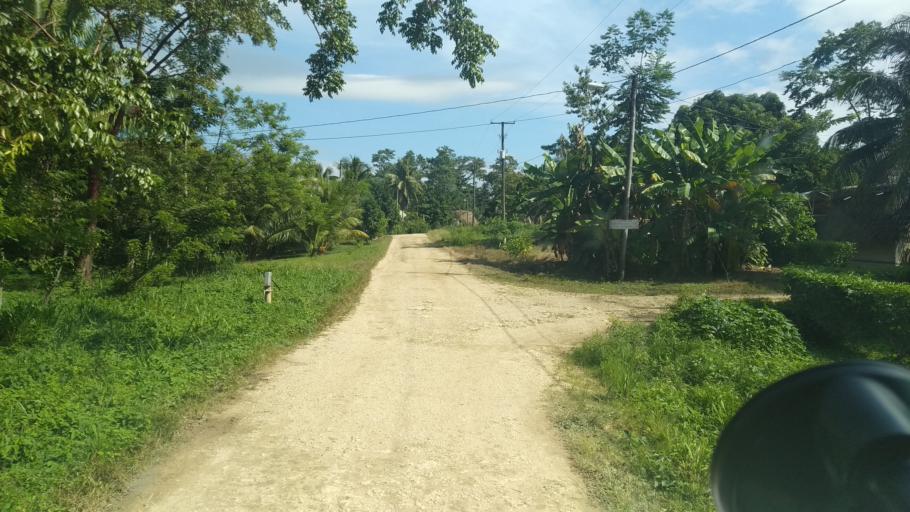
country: BZ
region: Toledo
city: Punta Gorda
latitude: 16.2180
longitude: -88.9021
